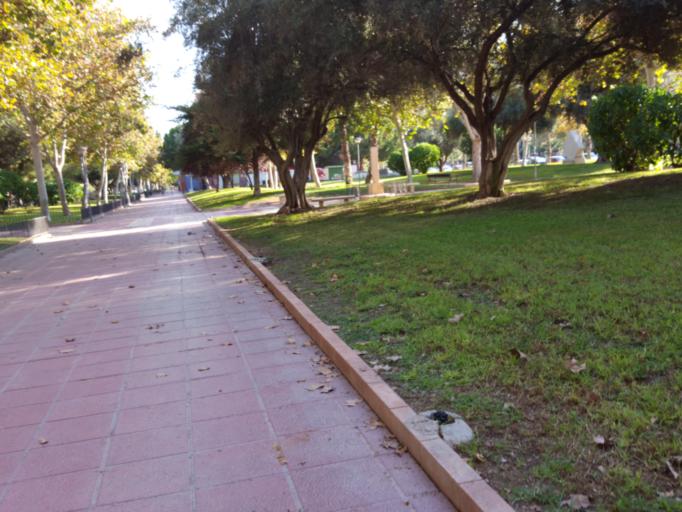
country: ES
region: Murcia
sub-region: Murcia
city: Murcia
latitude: 37.9964
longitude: -1.1249
